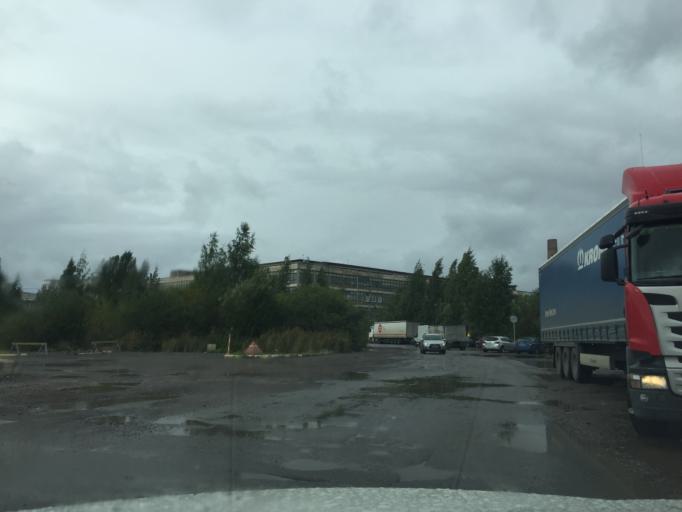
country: RU
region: St.-Petersburg
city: Sosnovaya Polyana
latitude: 59.8550
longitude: 30.1271
